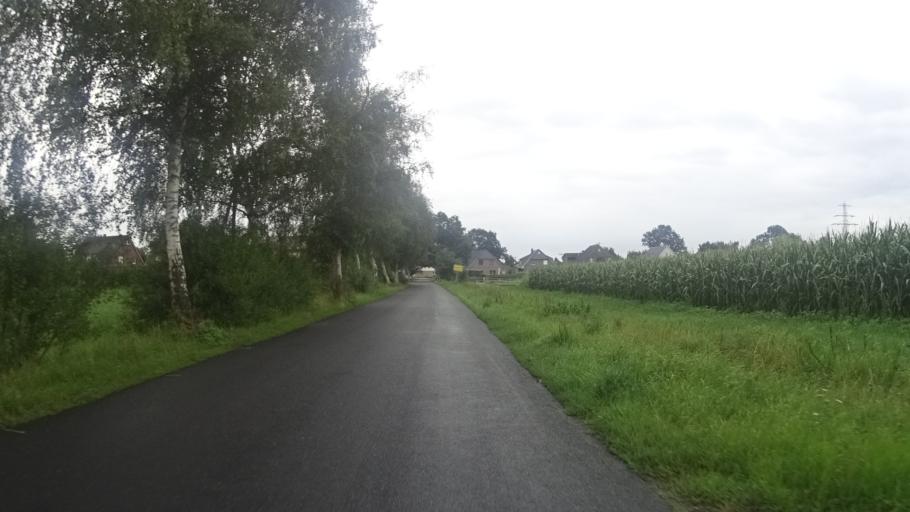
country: DE
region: Schleswig-Holstein
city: Kiebitzreihe
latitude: 53.7847
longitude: 9.6083
